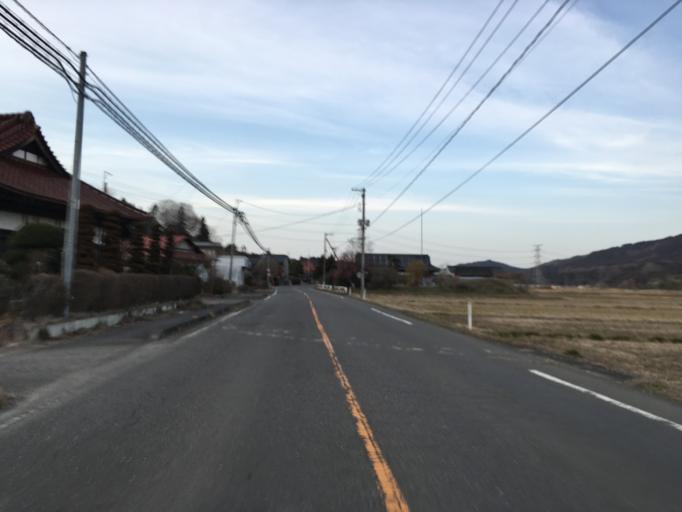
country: JP
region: Ibaraki
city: Daigo
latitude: 36.9198
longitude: 140.4079
